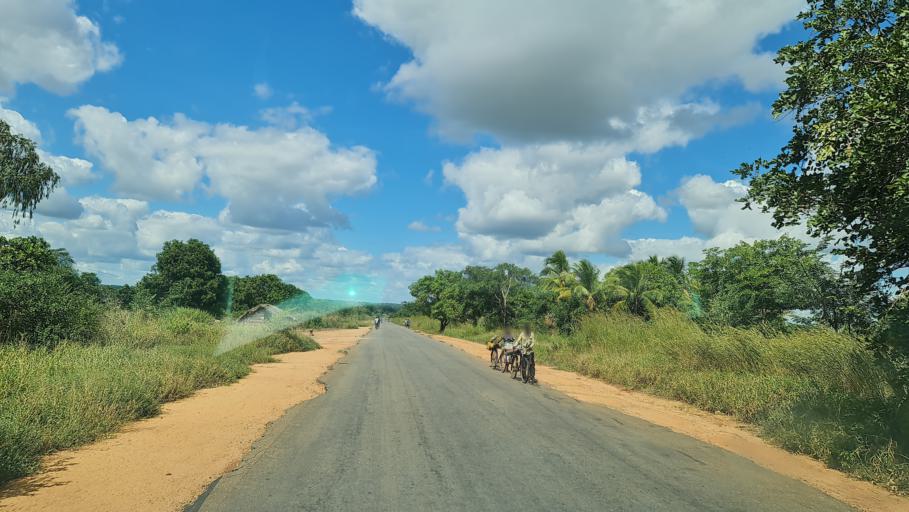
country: MZ
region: Zambezia
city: Quelimane
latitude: -17.5085
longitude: 36.2509
